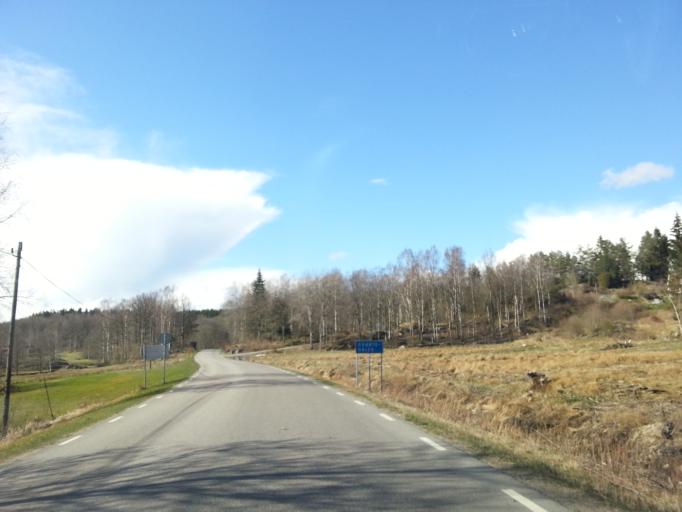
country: SE
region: Vaestra Goetaland
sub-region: Kungalvs Kommun
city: Diserod
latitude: 57.9582
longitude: 12.0161
